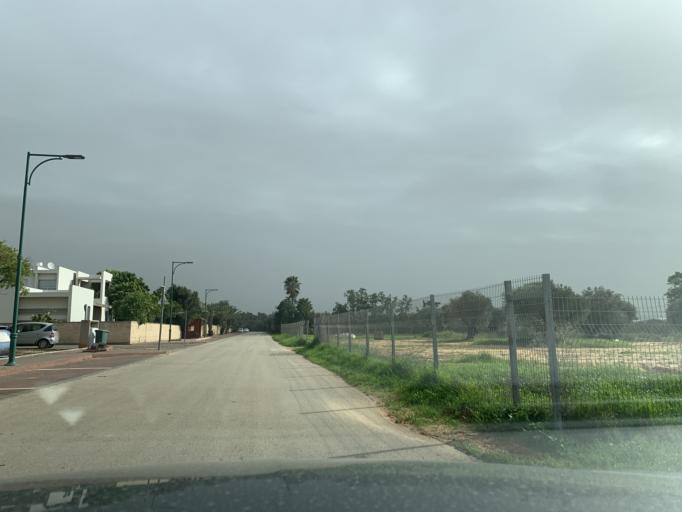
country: IL
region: Central District
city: Jaljulya
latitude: 32.1569
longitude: 34.9405
